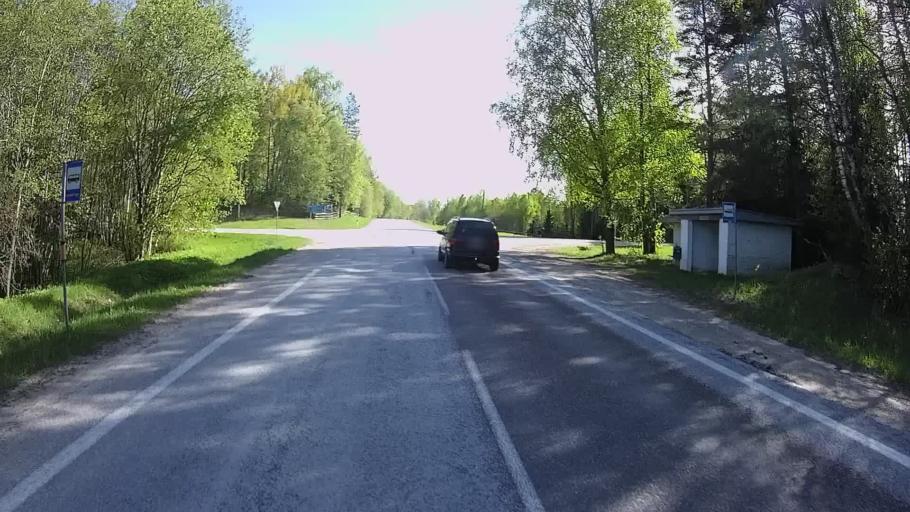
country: EE
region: Vorumaa
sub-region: Antsla vald
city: Vana-Antsla
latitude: 57.9970
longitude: 26.4952
